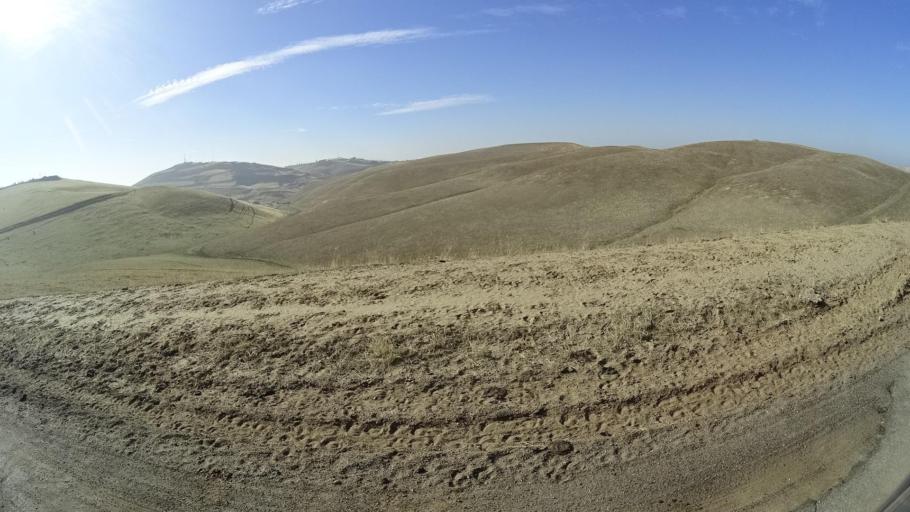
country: US
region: California
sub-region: Kern County
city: Oildale
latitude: 35.4933
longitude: -118.8738
